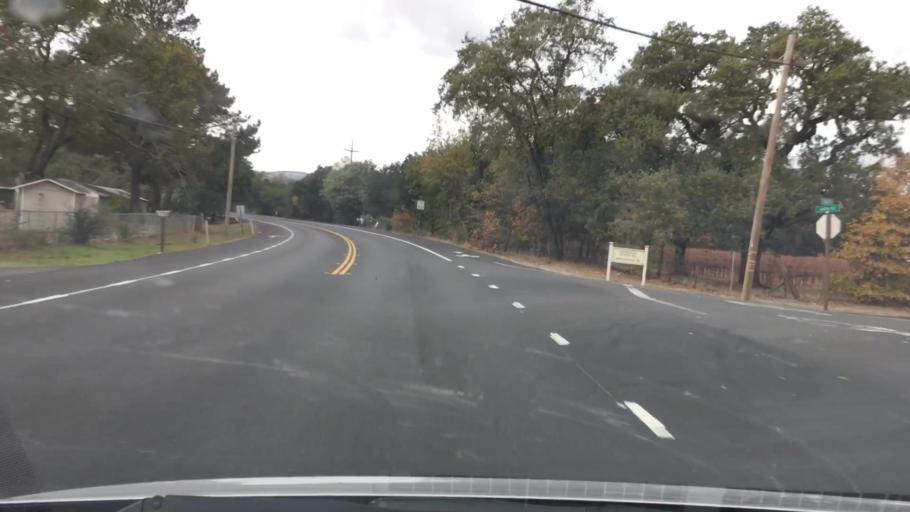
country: US
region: California
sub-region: Sonoma County
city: Sonoma
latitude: 38.2713
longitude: -122.4232
